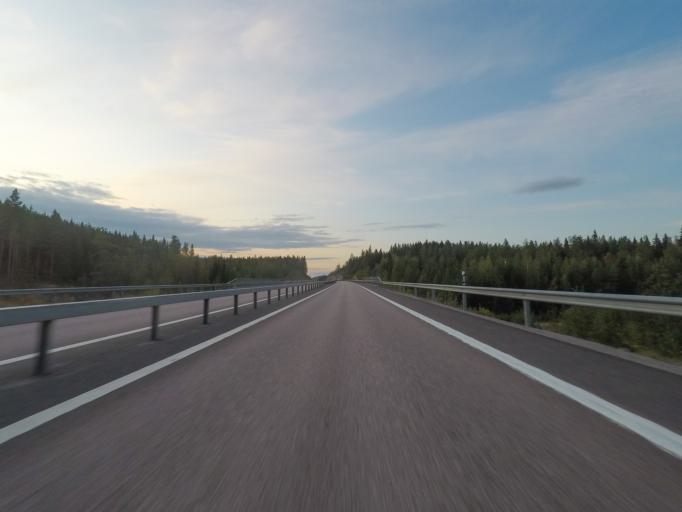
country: FI
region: Central Finland
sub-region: Jyvaeskylae
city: Saeynaetsalo
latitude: 62.1769
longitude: 25.9066
